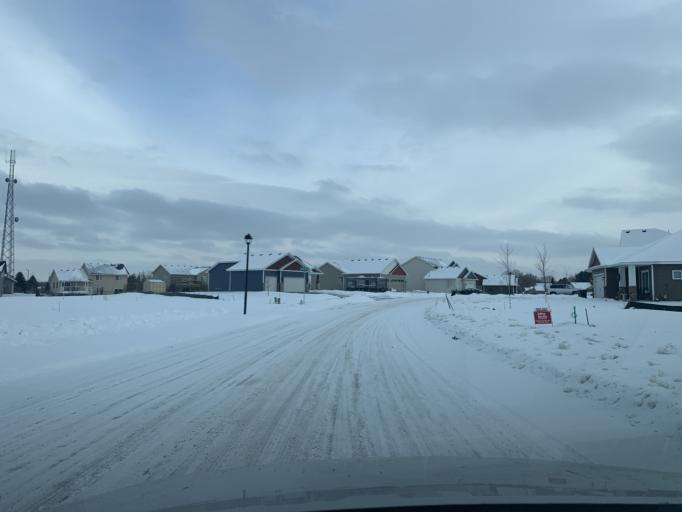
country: US
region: Minnesota
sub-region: Anoka County
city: Ramsey
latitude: 45.2467
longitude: -93.4123
